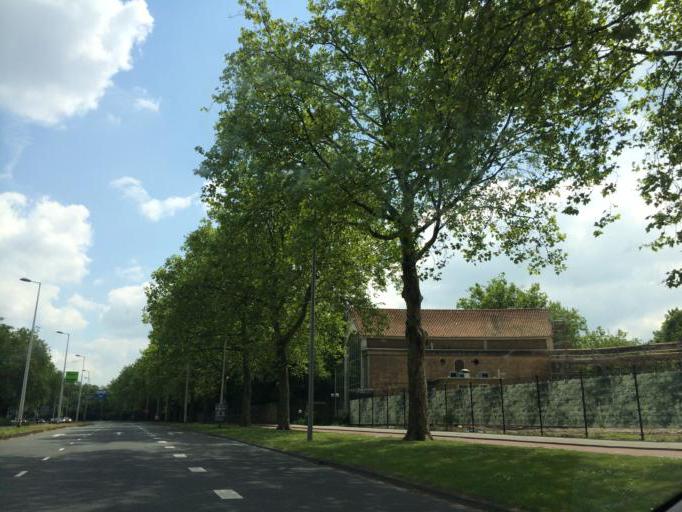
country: NL
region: South Holland
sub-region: Gemeente Rotterdam
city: Delfshaven
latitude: 51.9290
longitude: 4.4496
